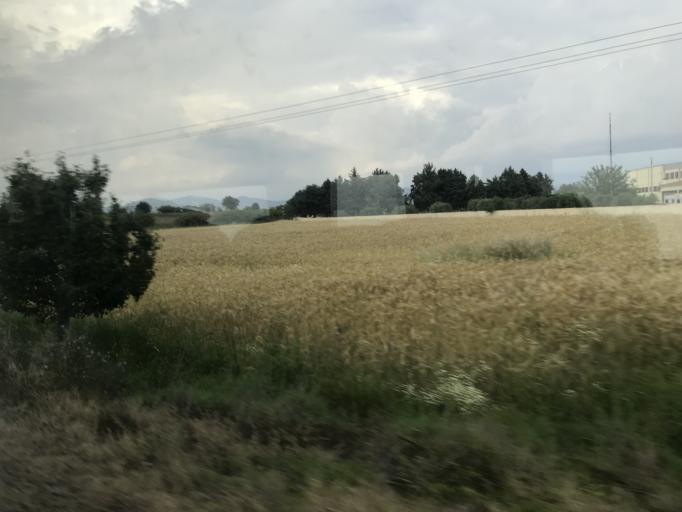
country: GR
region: East Macedonia and Thrace
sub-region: Nomos Rodopis
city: Sapes
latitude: 40.9750
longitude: 25.6451
